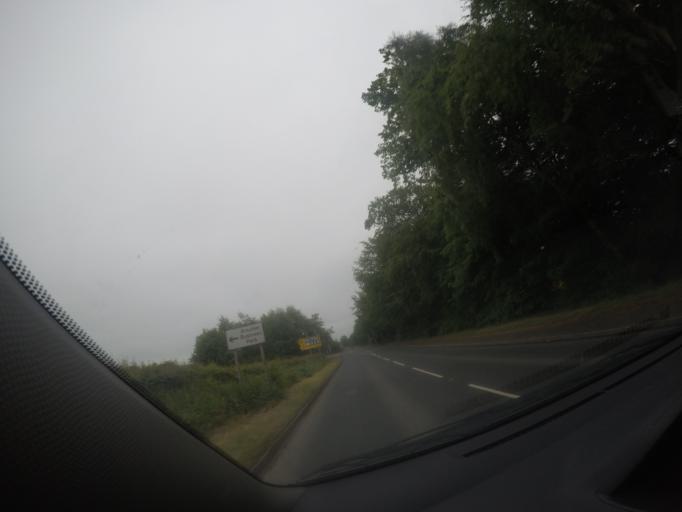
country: GB
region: Scotland
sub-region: Angus
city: Brechin
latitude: 56.7299
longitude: -2.6838
